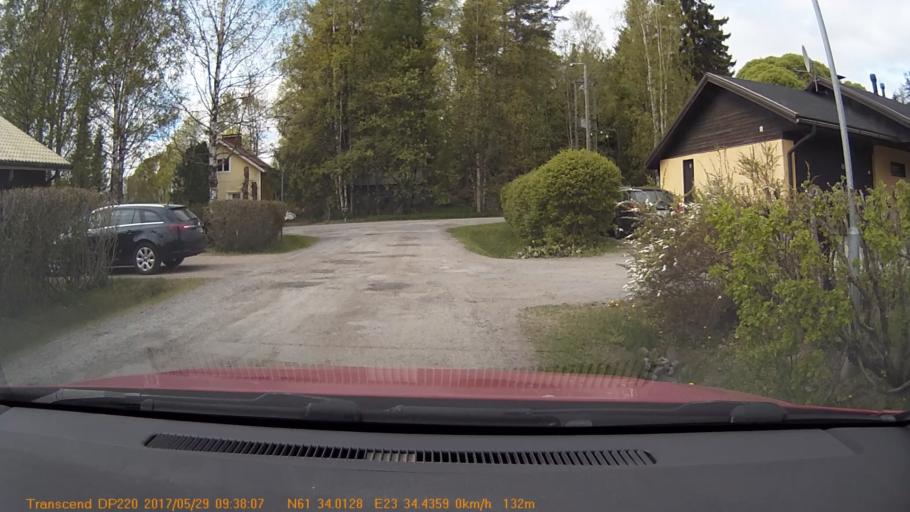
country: FI
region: Pirkanmaa
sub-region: Tampere
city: Yloejaervi
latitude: 61.5669
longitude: 23.5740
